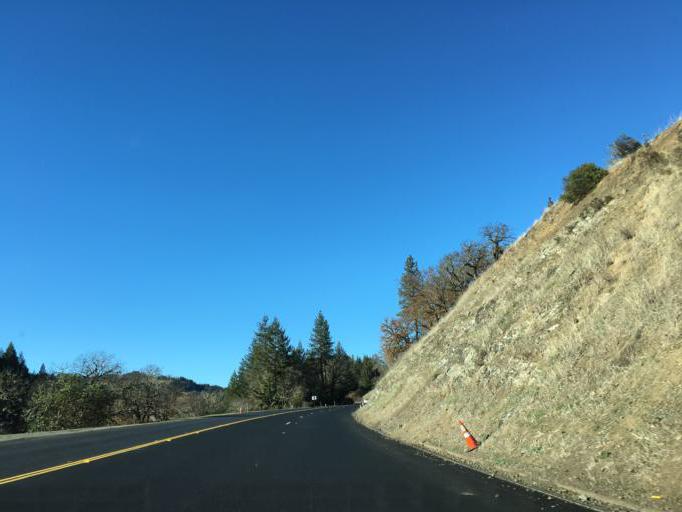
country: US
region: California
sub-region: Mendocino County
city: Laytonville
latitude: 39.7509
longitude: -123.5344
